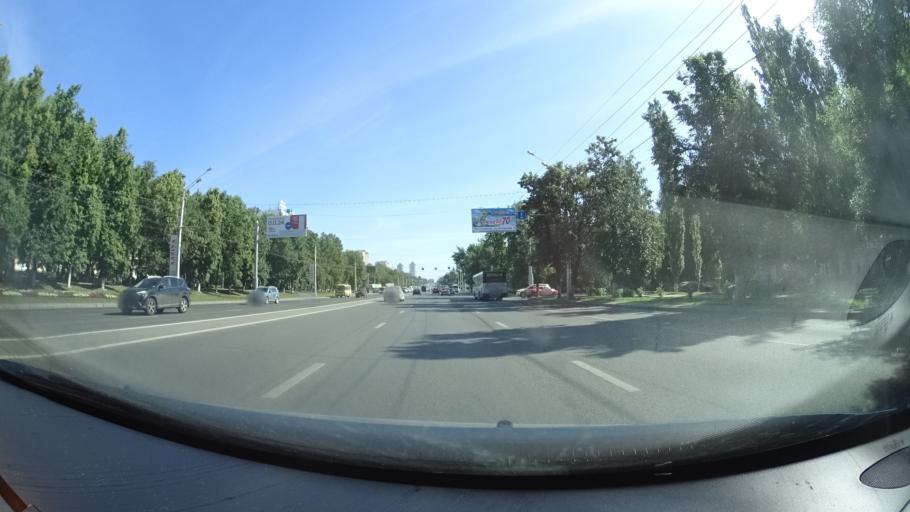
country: RU
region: Bashkortostan
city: Ufa
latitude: 54.7537
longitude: 56.0025
